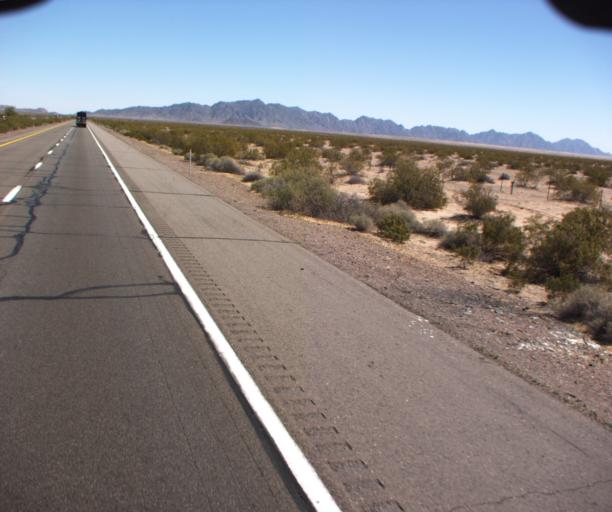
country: US
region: Arizona
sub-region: Yuma County
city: Wellton
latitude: 32.7083
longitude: -113.8552
